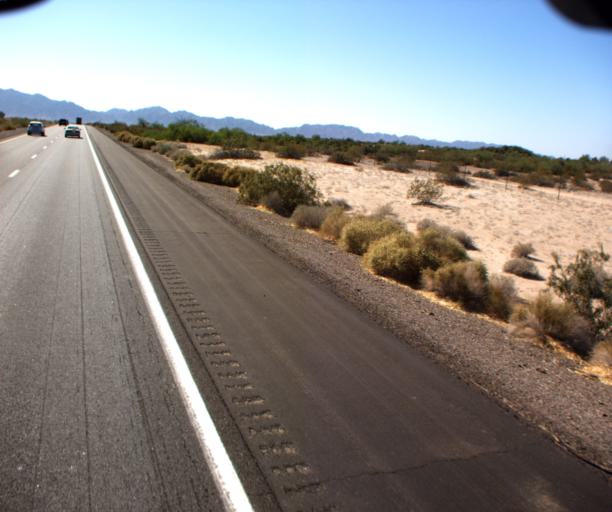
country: US
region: Arizona
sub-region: Yuma County
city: Wellton
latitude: 32.6560
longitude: -114.1677
